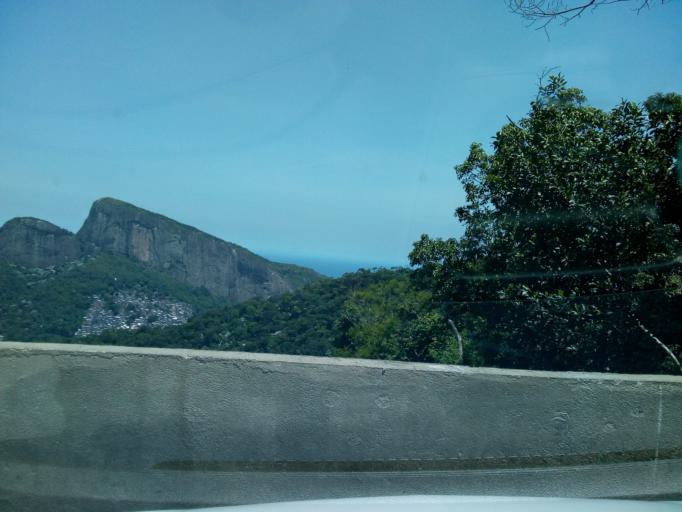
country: BR
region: Rio de Janeiro
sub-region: Rio De Janeiro
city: Rio de Janeiro
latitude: -22.9734
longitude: -43.2499
